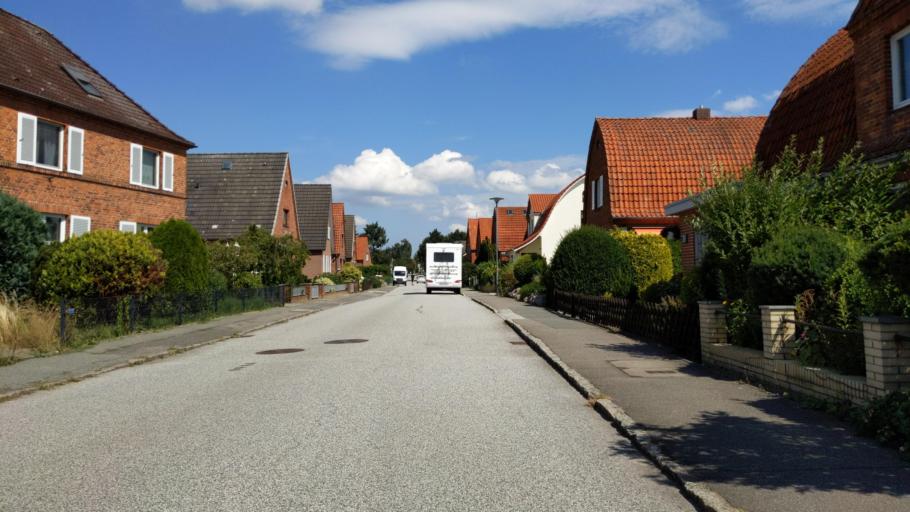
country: DE
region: Schleswig-Holstein
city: Luebeck
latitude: 53.8383
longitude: 10.6785
